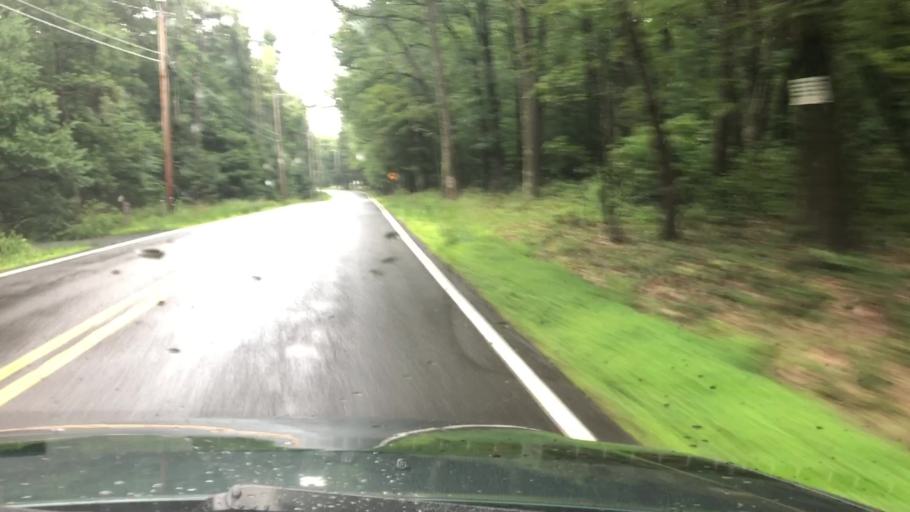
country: US
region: Pennsylvania
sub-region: Wayne County
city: Hawley
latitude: 41.3270
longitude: -75.2066
